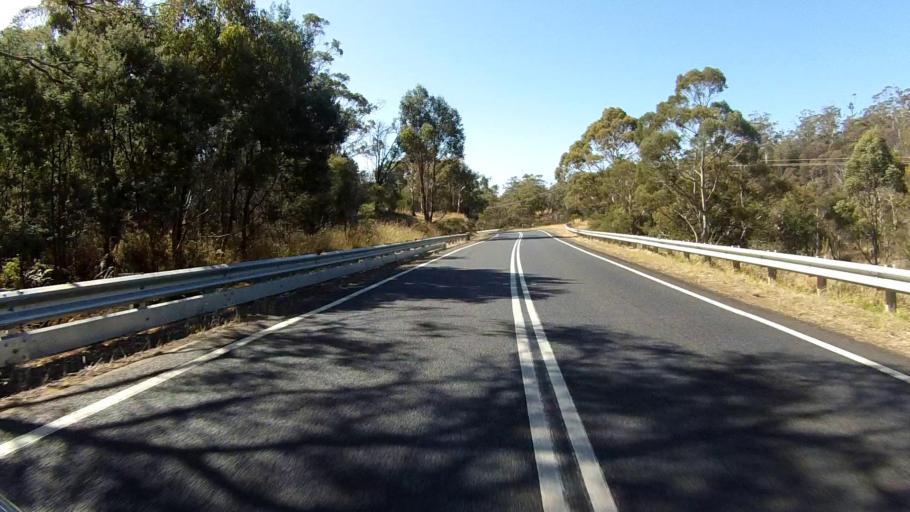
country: AU
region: Tasmania
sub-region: Sorell
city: Sorell
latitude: -42.3933
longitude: 147.9332
